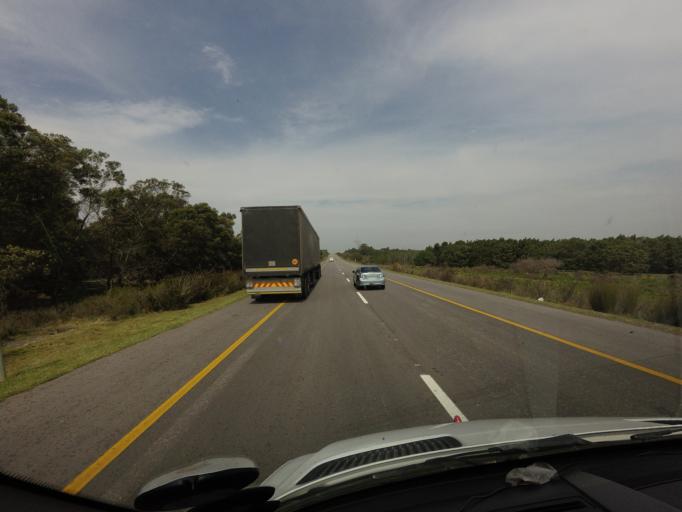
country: ZA
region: Eastern Cape
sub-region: Cacadu District Municipality
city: Kruisfontein
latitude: -33.9957
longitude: 24.7408
